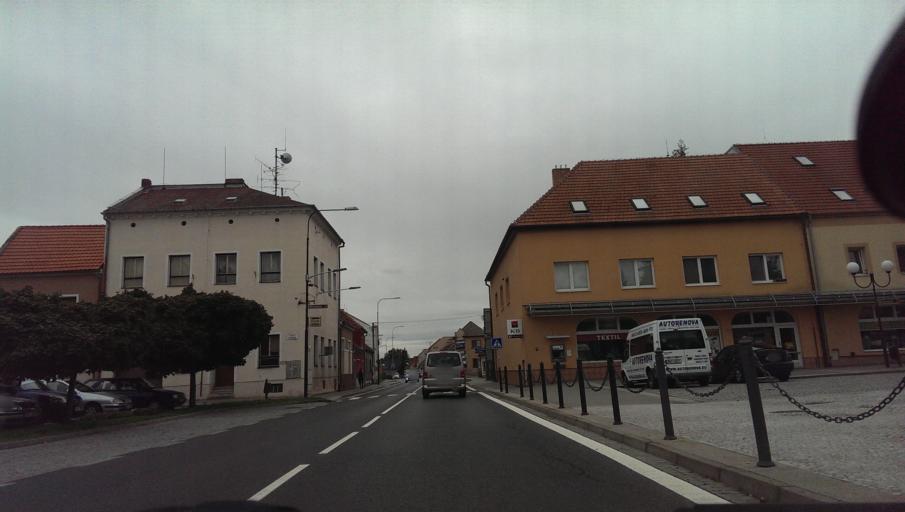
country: CZ
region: South Moravian
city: Bzenec
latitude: 48.9733
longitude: 17.2648
